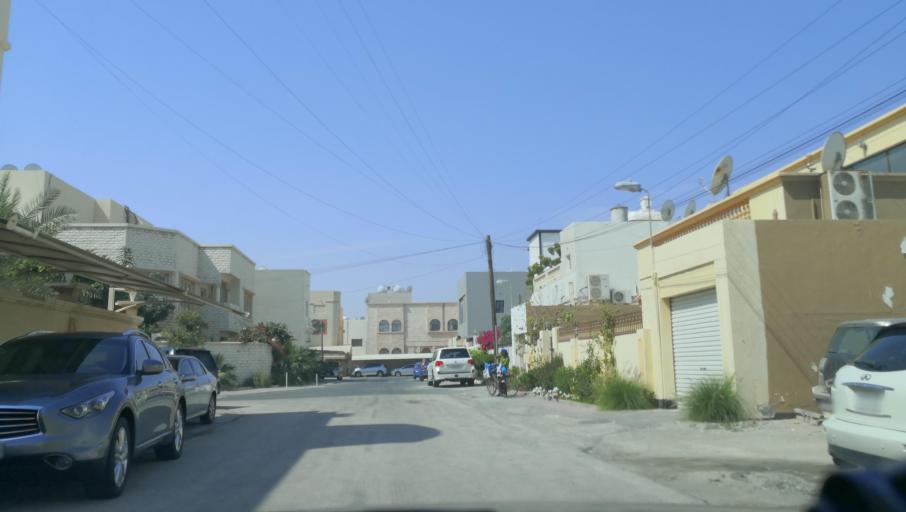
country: BH
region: Muharraq
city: Al Hadd
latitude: 26.2524
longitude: 50.6469
